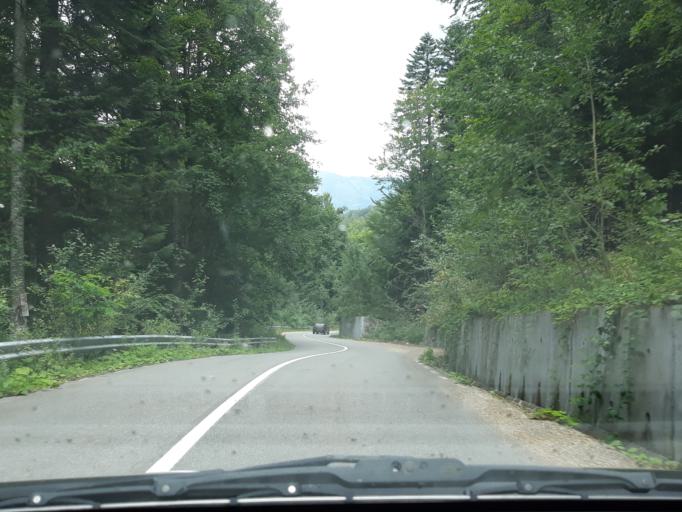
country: RO
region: Bihor
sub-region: Comuna Pietroasa
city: Pietroasa
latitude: 46.5945
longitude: 22.6710
